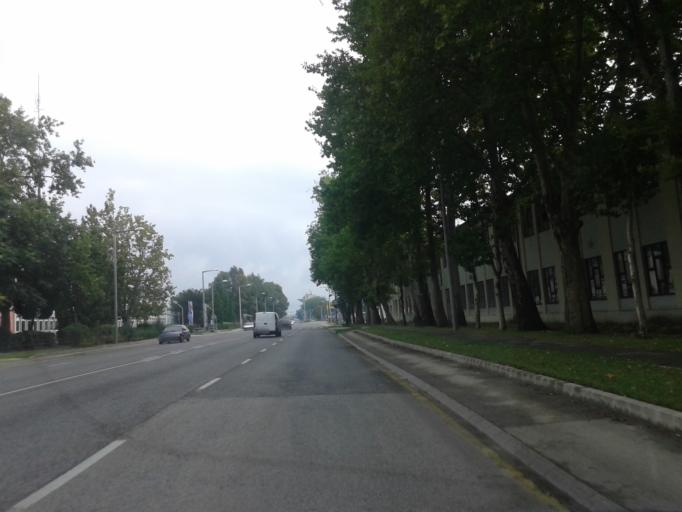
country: HU
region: Csongrad
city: Szeged
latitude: 46.2569
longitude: 20.1254
